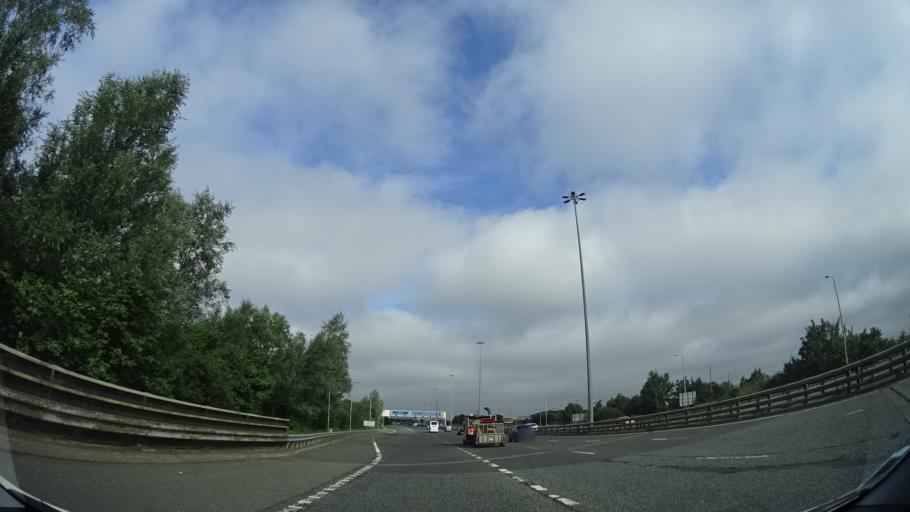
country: GB
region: Scotland
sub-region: Renfrewshire
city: Renfrew
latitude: 55.8630
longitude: -4.3545
